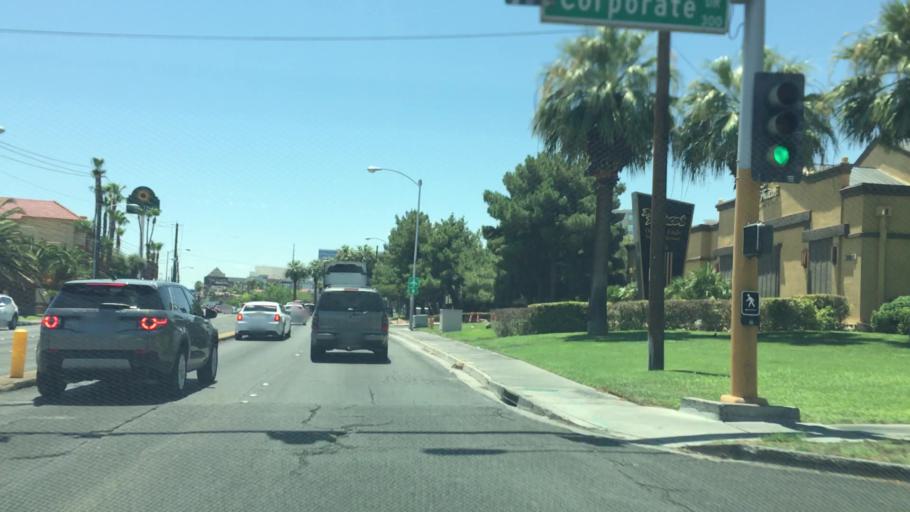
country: US
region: Nevada
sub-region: Clark County
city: Paradise
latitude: 36.1184
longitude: -115.1551
